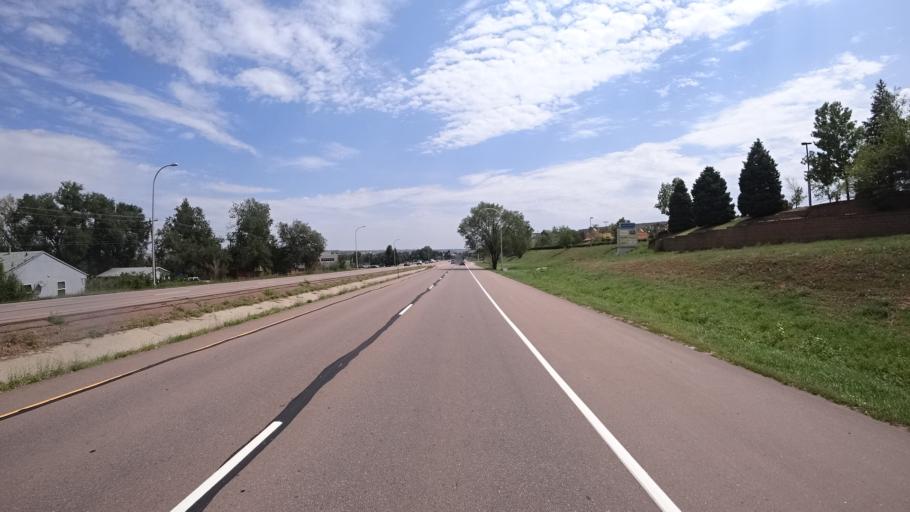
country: US
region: Colorado
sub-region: El Paso County
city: Colorado Springs
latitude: 38.7972
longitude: -104.8138
